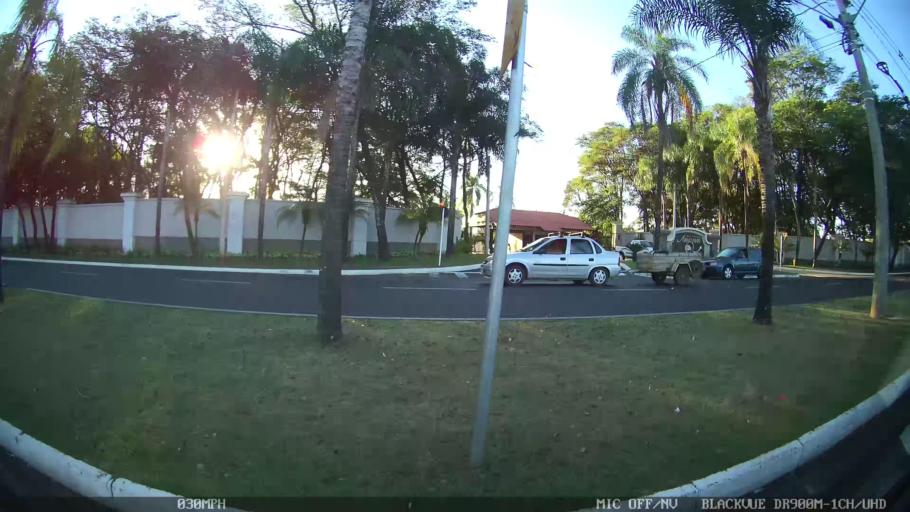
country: BR
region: Sao Paulo
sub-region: Sao Jose Do Rio Preto
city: Sao Jose do Rio Preto
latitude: -20.7651
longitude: -49.3520
